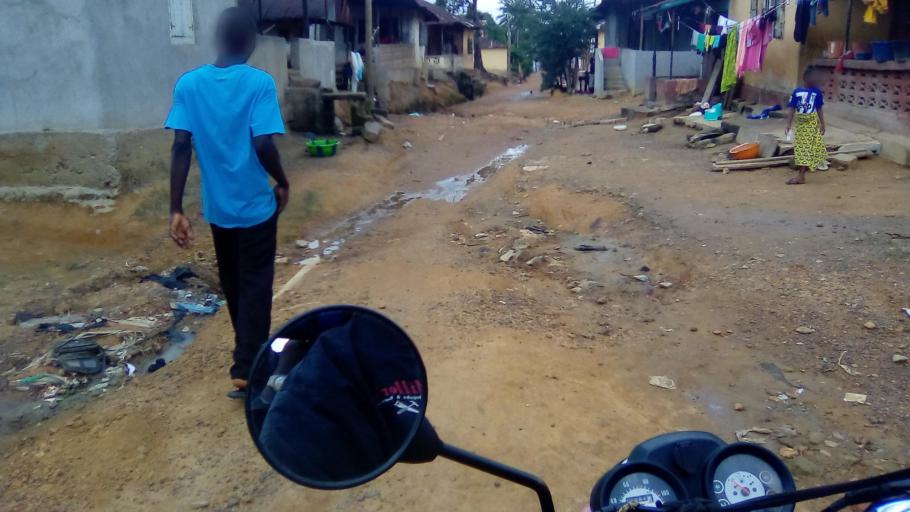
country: SL
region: Southern Province
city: Bo
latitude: 7.9567
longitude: -11.7493
